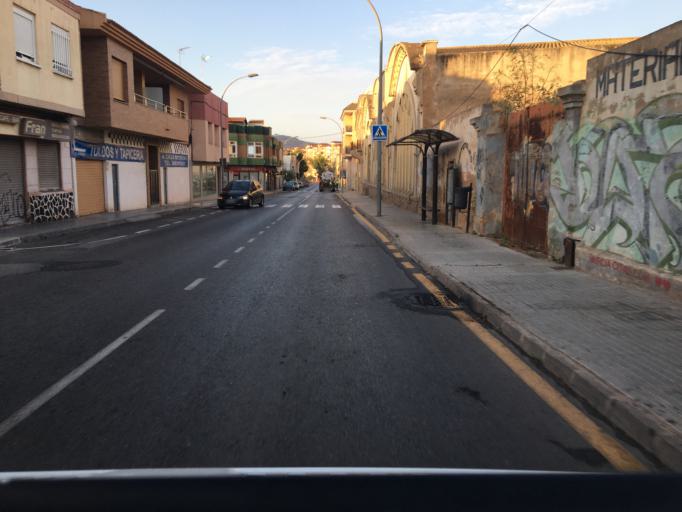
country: ES
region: Murcia
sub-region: Murcia
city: Cartagena
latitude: 37.6198
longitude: -0.9886
